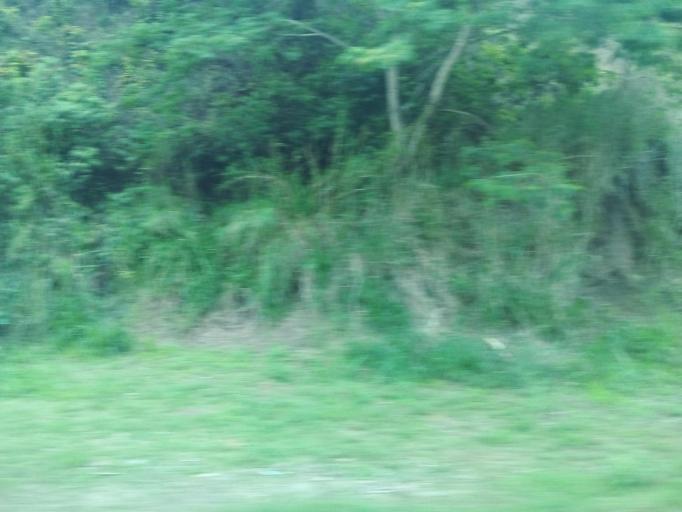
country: BR
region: Minas Gerais
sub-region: Joao Monlevade
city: Joao Monlevade
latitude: -19.8080
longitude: -43.1039
